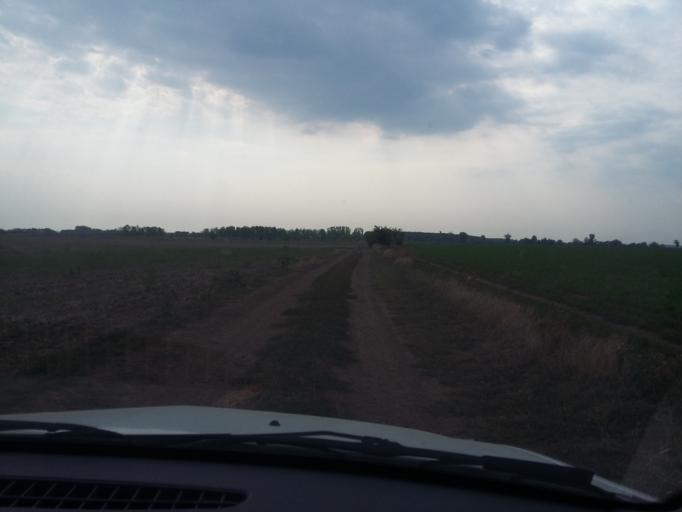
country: HU
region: Borsod-Abauj-Zemplen
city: Taktaszada
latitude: 48.1296
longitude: 21.1980
